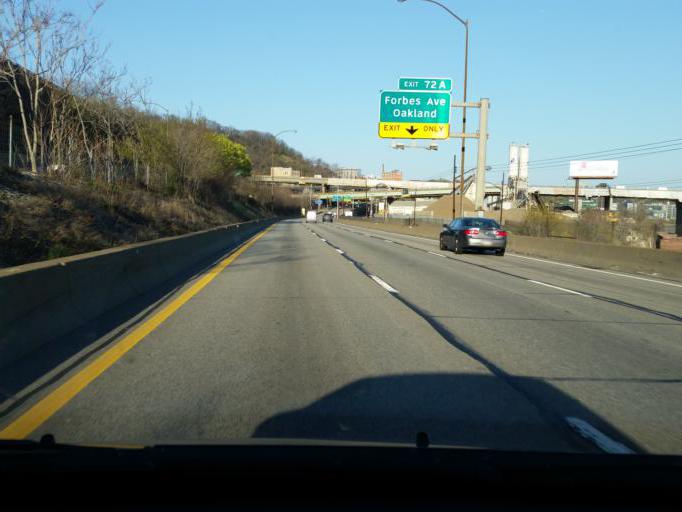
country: US
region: Pennsylvania
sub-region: Allegheny County
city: Pittsburgh
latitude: 40.4355
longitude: -79.9792
